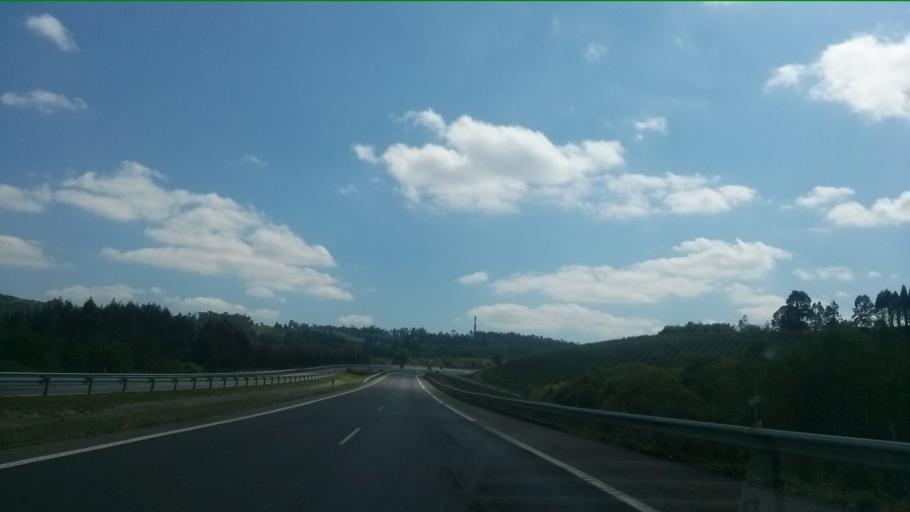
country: ES
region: Galicia
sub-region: Provincia da Coruna
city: Oroso
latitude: 42.9082
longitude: -8.4624
